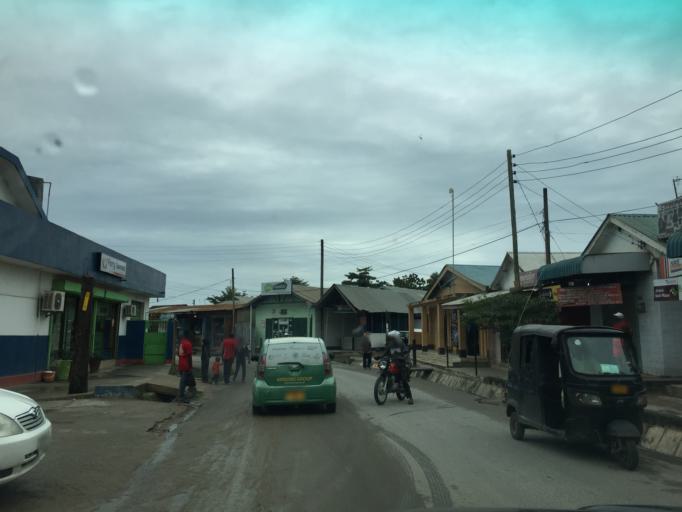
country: TZ
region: Dar es Salaam
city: Dar es Salaam
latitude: -6.8236
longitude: 39.3034
